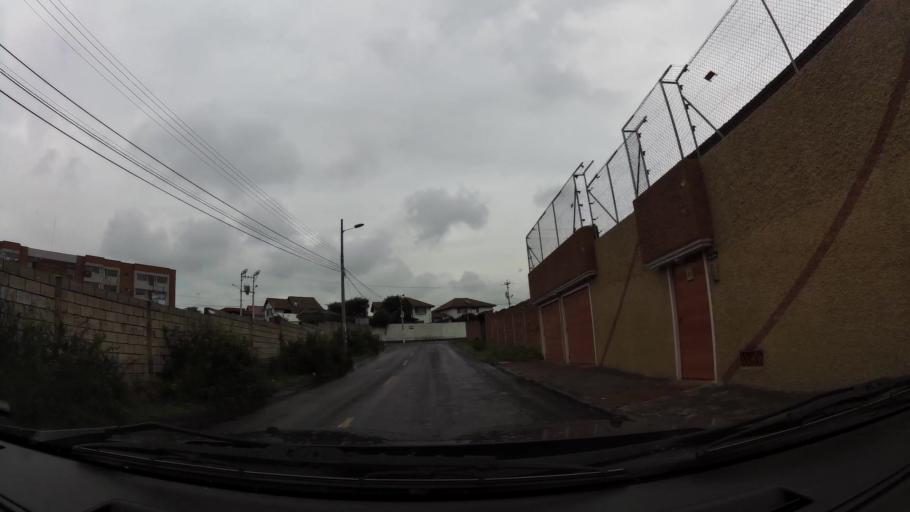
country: EC
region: Pichincha
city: Sangolqui
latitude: -0.2972
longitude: -78.4453
